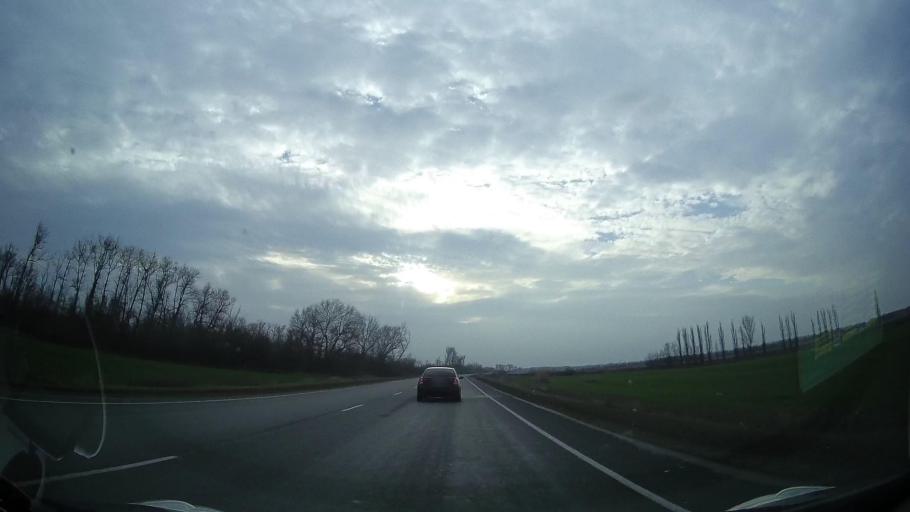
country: RU
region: Rostov
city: Ol'ginskaya
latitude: 47.1359
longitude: 39.9893
